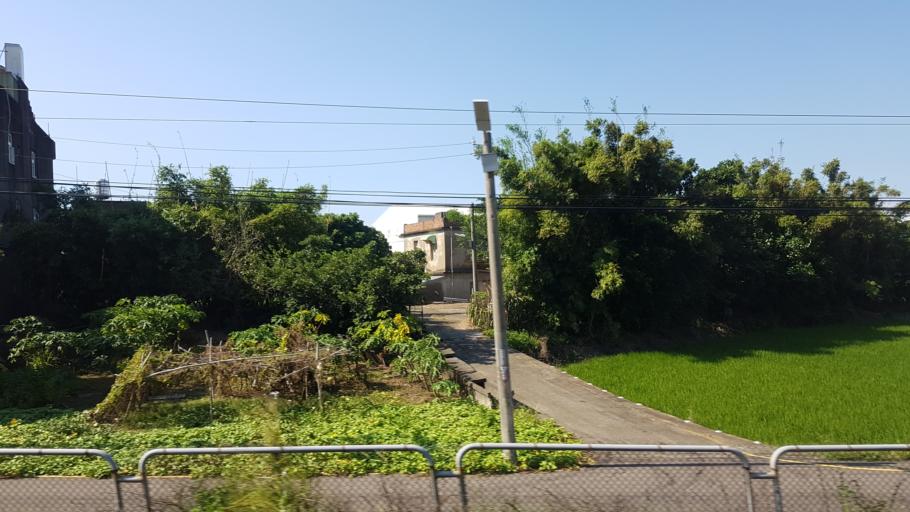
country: TW
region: Taiwan
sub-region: Hsinchu
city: Hsinchu
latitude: 24.7399
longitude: 120.8980
